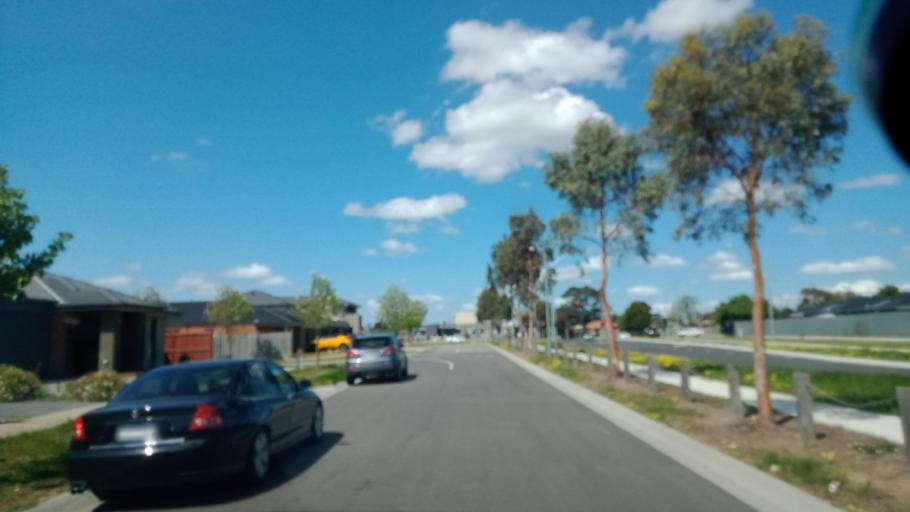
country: AU
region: Victoria
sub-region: Casey
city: Cranbourne West
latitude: -38.1017
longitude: 145.2522
